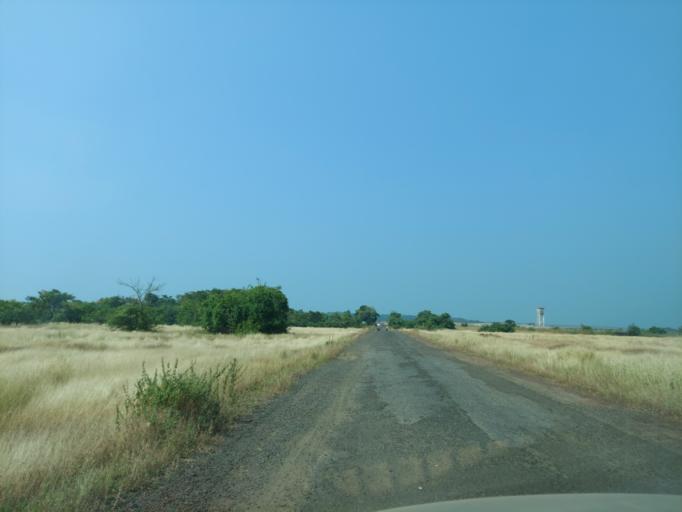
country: IN
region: Maharashtra
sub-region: Sindhudurg
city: Malvan
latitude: 15.9977
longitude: 73.5166
